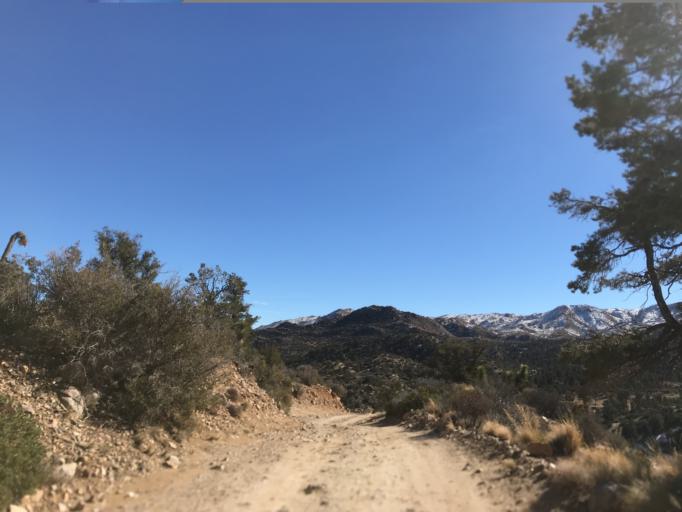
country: US
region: California
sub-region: San Bernardino County
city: Big Bear City
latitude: 34.2289
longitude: -116.6764
